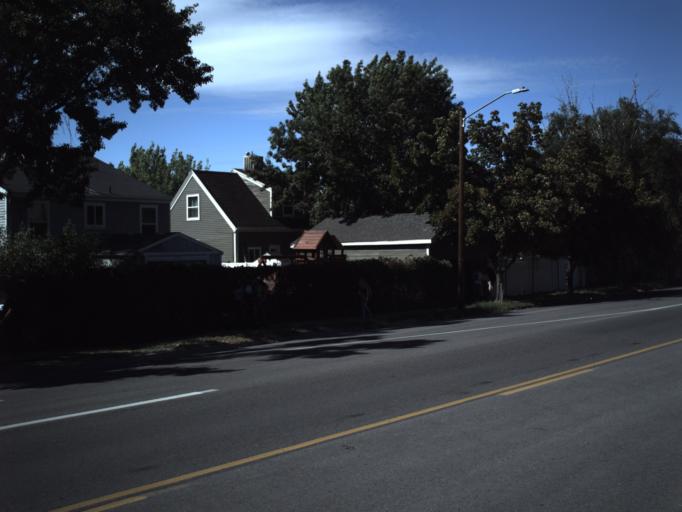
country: US
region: Utah
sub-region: Davis County
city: North Salt Lake
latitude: 40.8030
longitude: -111.9391
